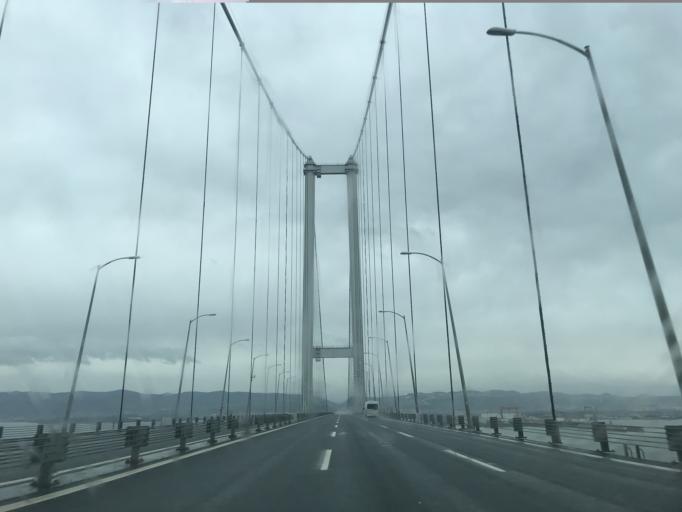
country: TR
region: Yalova
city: Altinova
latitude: 40.7516
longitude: 29.5152
